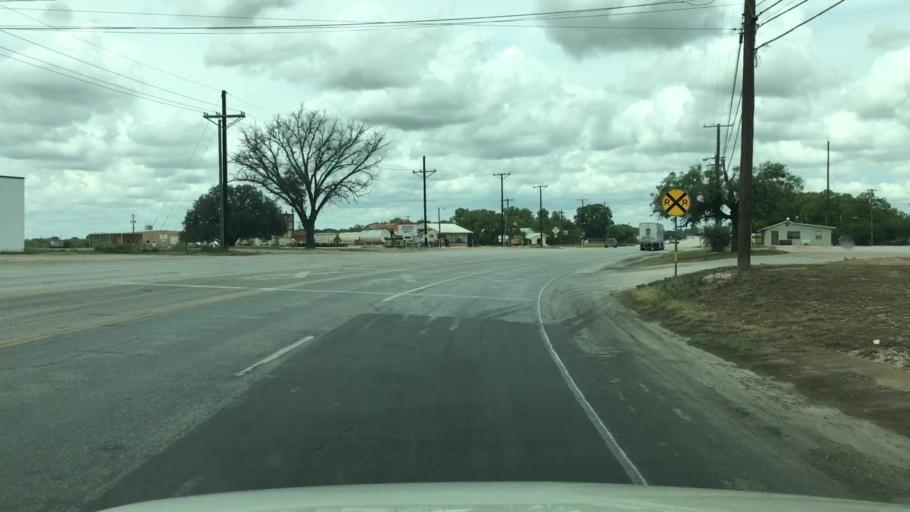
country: US
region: Texas
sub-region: McCulloch County
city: Brady
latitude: 31.1374
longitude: -99.3461
